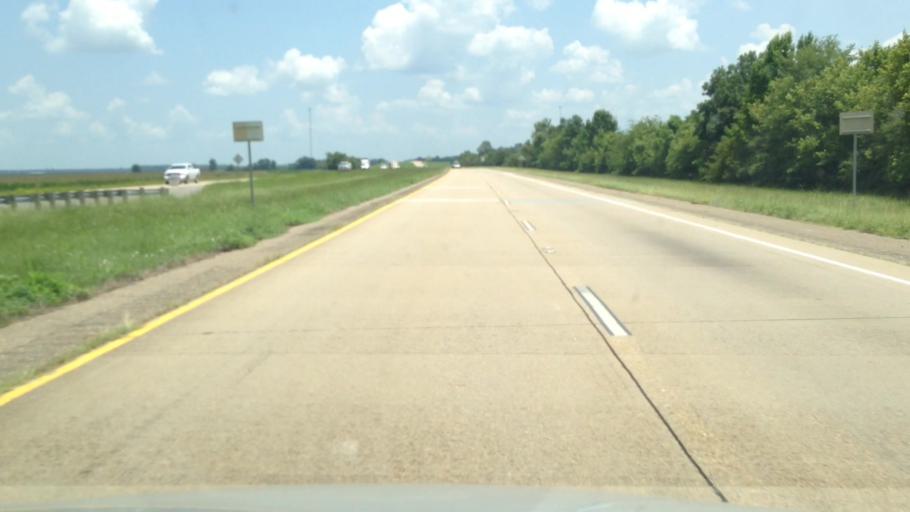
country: US
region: Louisiana
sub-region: Rapides Parish
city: Lecompte
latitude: 31.0196
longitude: -92.3885
